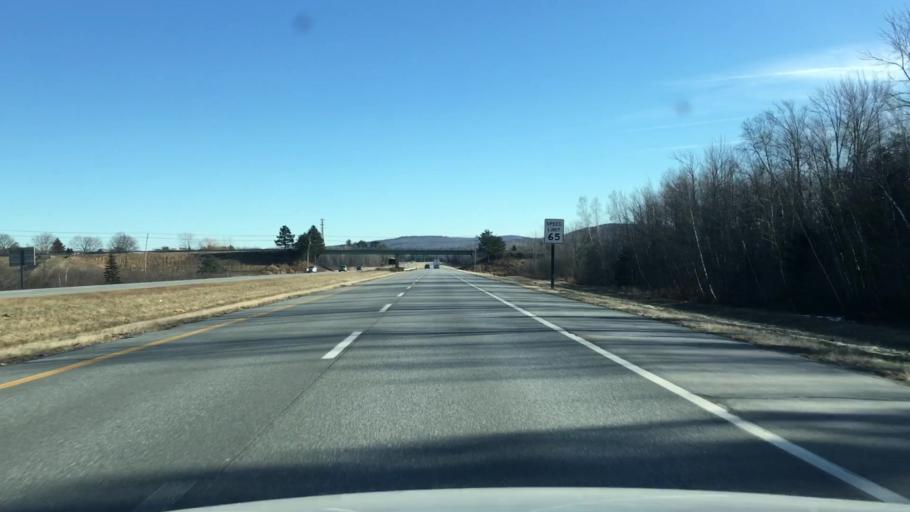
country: US
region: Maine
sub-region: Penobscot County
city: Brewer
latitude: 44.7756
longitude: -68.7494
